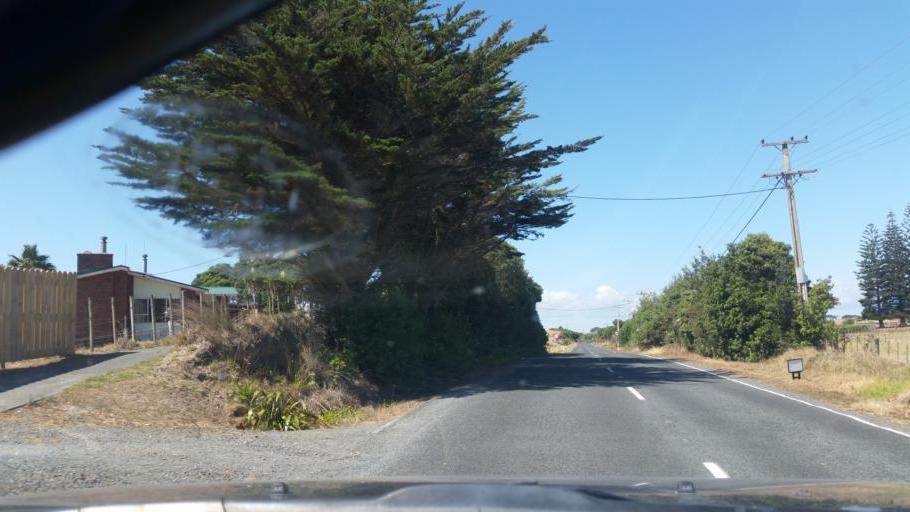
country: NZ
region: Northland
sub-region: Kaipara District
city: Dargaville
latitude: -35.9508
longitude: 173.7521
